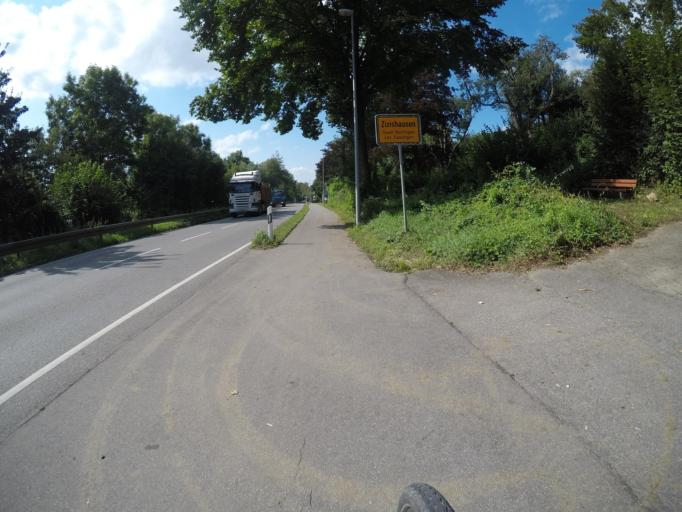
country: DE
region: Baden-Wuerttemberg
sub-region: Regierungsbezirk Stuttgart
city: Unterensingen
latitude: 48.6469
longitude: 9.3512
